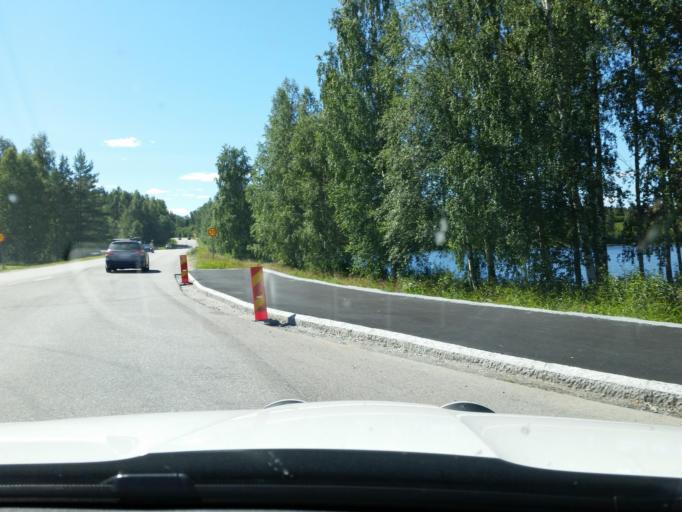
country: SE
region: Norrbotten
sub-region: Pitea Kommun
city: Bergsviken
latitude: 65.3132
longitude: 21.4000
